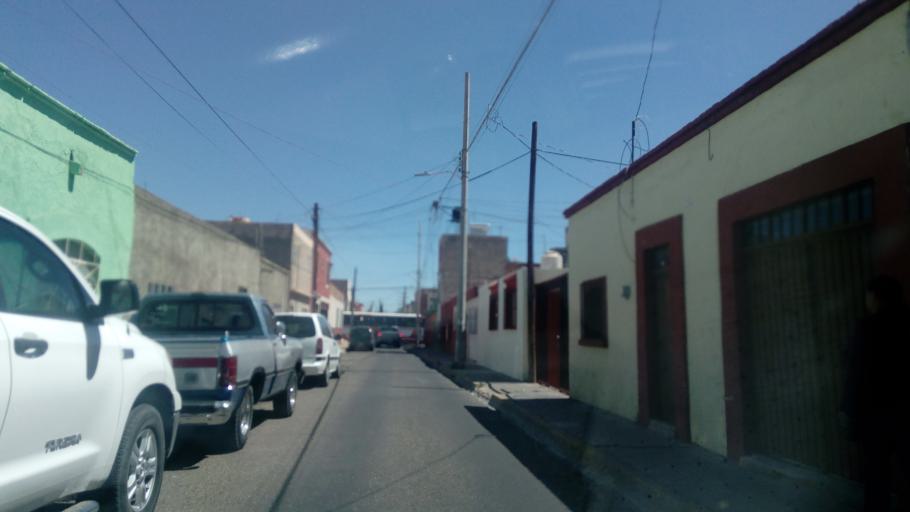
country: MX
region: Durango
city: Victoria de Durango
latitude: 24.0295
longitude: -104.6596
